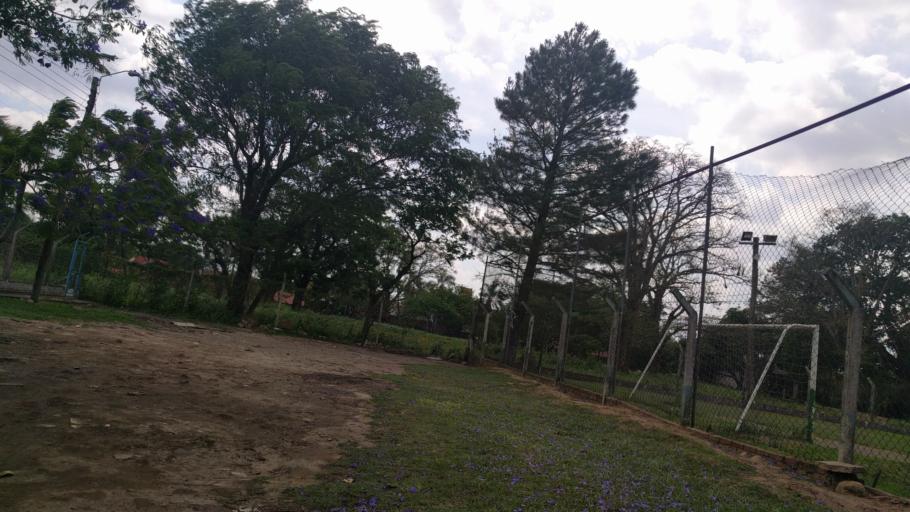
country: BO
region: Santa Cruz
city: Santa Cruz de la Sierra
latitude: -17.7876
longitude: -63.2201
